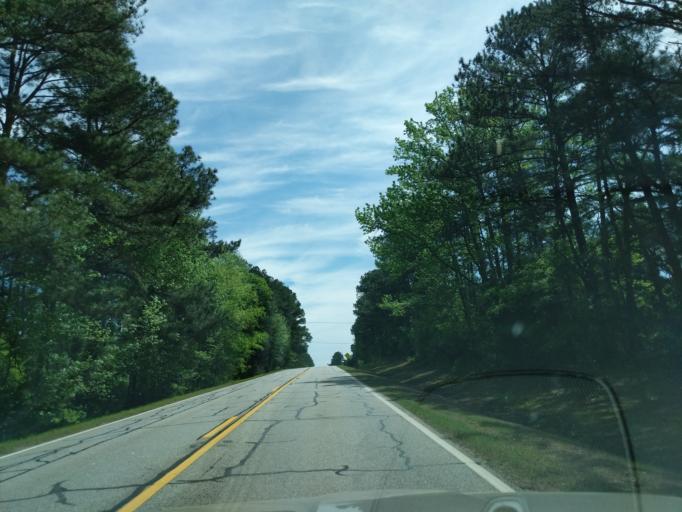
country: US
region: Georgia
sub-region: Columbia County
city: Appling
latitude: 33.6116
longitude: -82.3546
